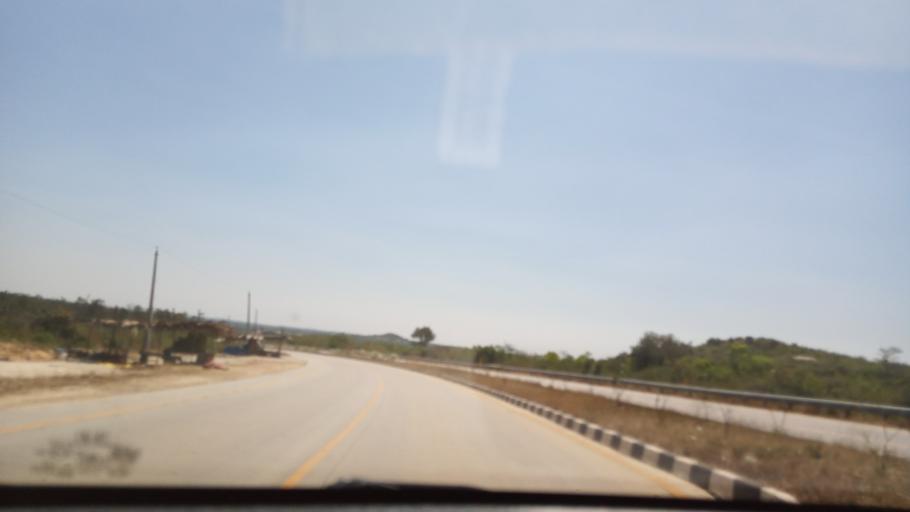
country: IN
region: Andhra Pradesh
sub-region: Chittoor
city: Palmaner
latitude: 13.1812
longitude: 78.6445
